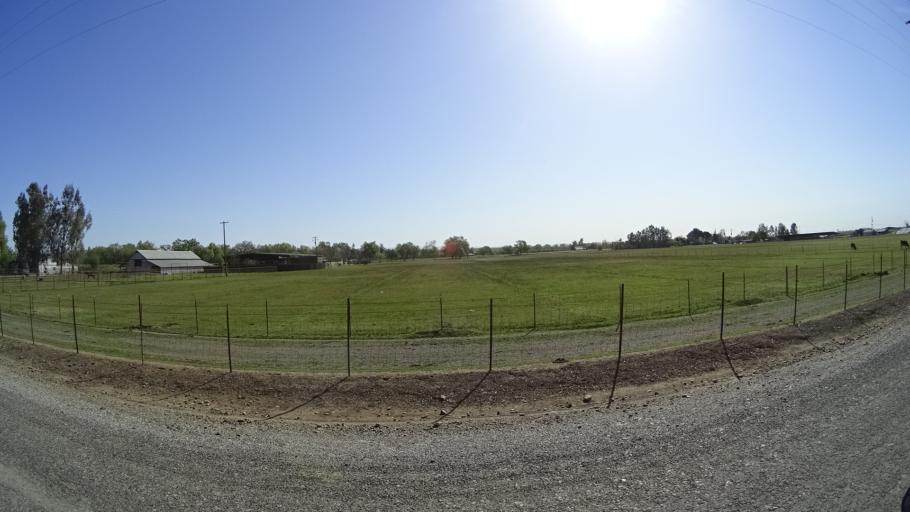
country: US
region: California
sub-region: Glenn County
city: Hamilton City
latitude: 39.7848
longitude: -122.0525
